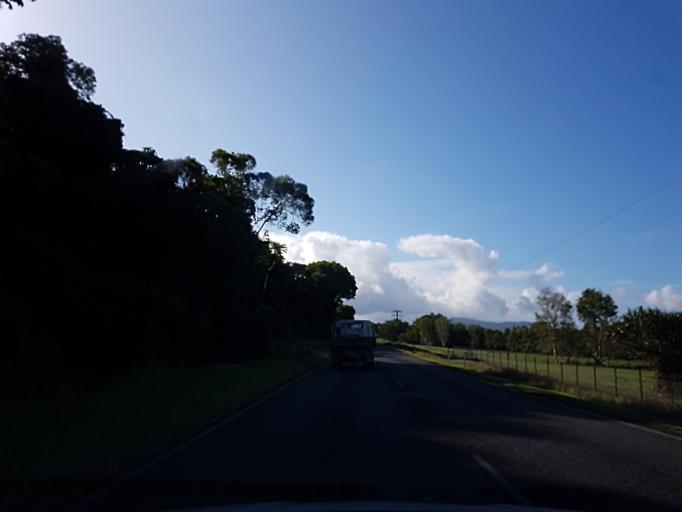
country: AU
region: Queensland
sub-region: Cairns
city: Port Douglas
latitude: -16.3286
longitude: 145.4089
